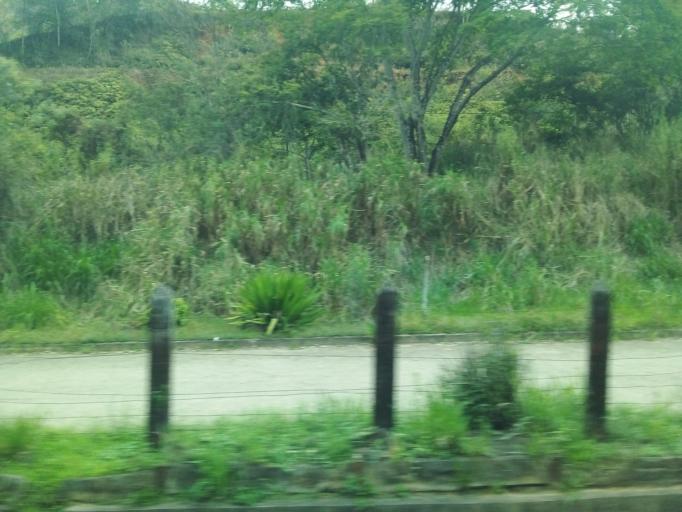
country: BR
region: Minas Gerais
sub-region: Nova Era
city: Nova Era
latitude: -19.7262
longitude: -42.9935
